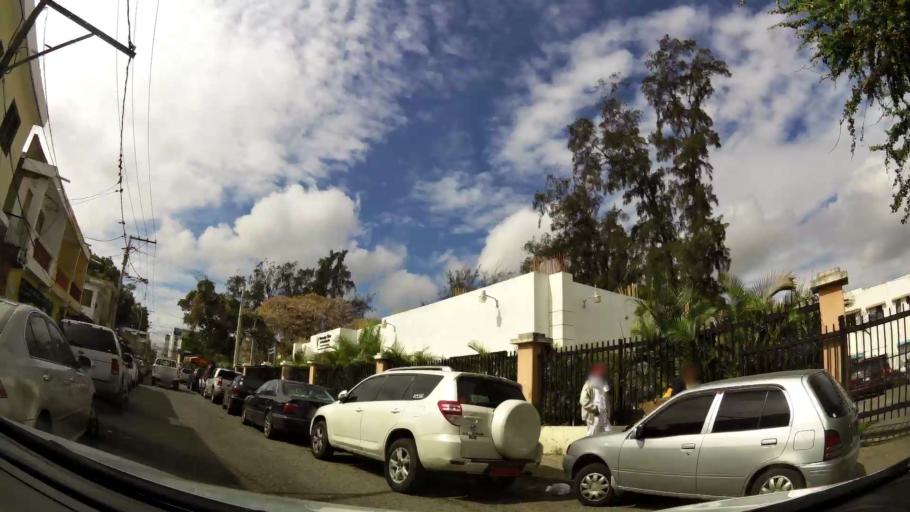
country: DO
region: Santiago
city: Santiago de los Caballeros
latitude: 19.4551
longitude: -70.6991
